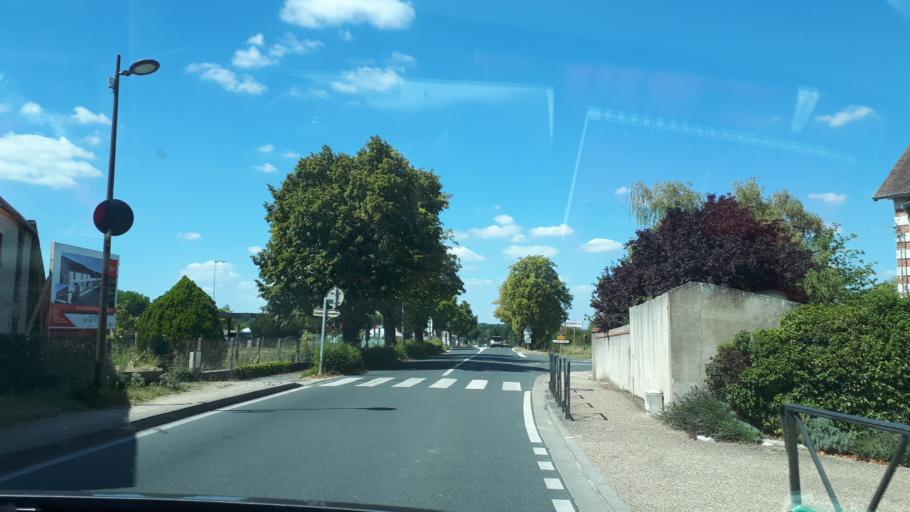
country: FR
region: Centre
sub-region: Departement du Loir-et-Cher
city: Mont-pres-Chambord
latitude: 47.5625
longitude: 1.4520
